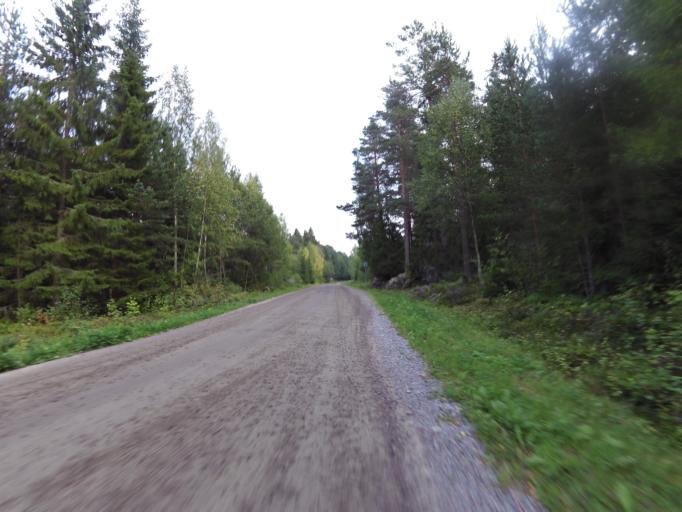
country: SE
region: Gaevleborg
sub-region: Gavle Kommun
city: Gavle
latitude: 60.7085
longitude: 17.1430
